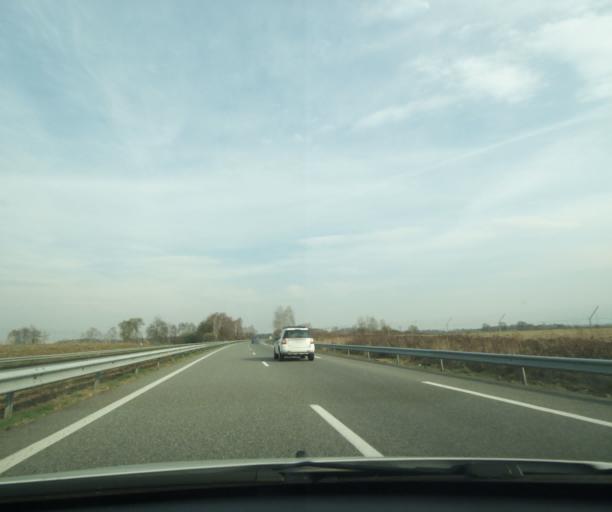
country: FR
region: Aquitaine
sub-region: Departement des Pyrenees-Atlantiques
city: Ger
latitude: 43.2441
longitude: -0.1067
